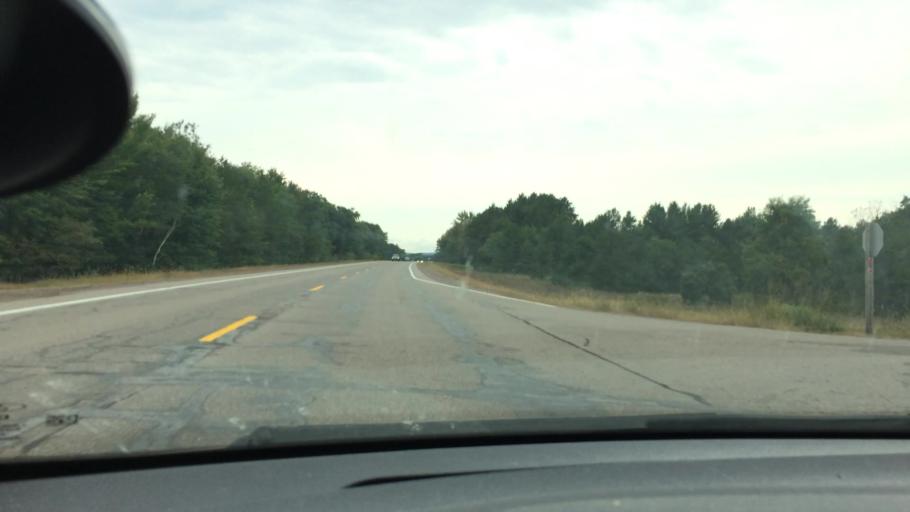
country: US
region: Wisconsin
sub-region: Eau Claire County
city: Augusta
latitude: 44.5814
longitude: -91.0797
